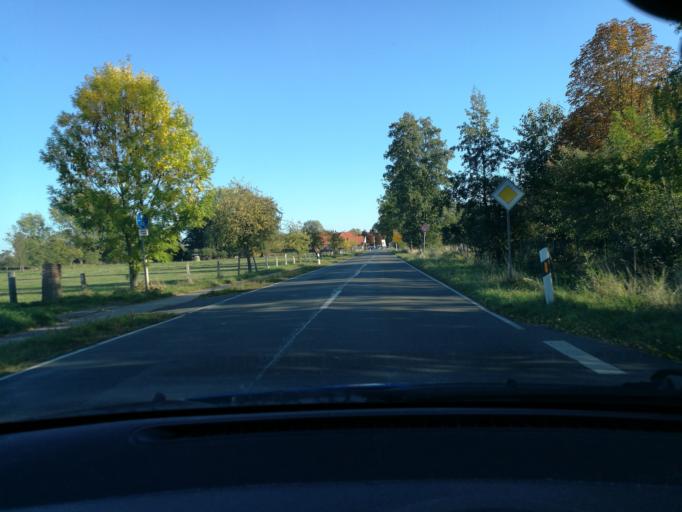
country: DE
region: Lower Saxony
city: Bleckede
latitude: 53.2997
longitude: 10.7119
